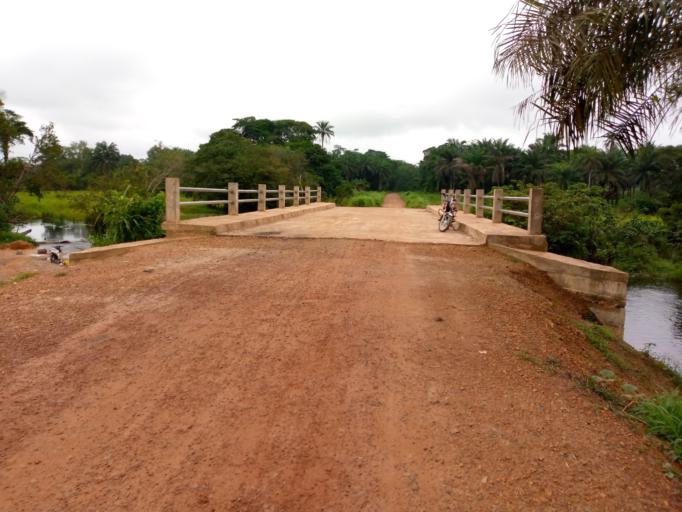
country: SL
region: Southern Province
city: Sumbuya
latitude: 7.5617
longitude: -12.0856
